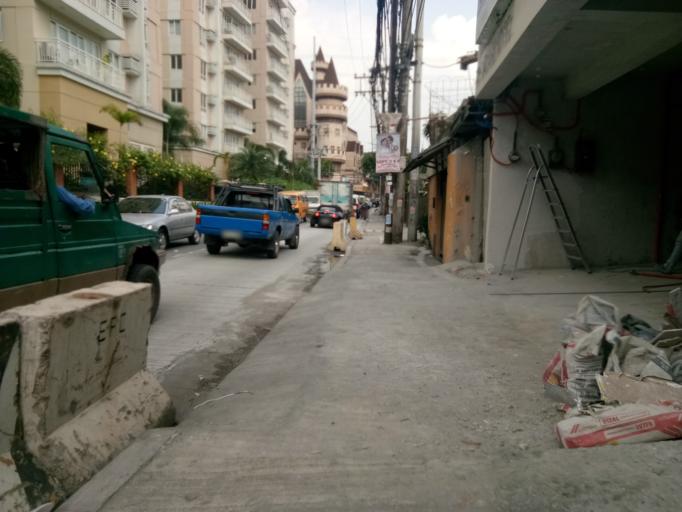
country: PH
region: Metro Manila
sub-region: San Juan
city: San Juan
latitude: 14.6141
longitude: 121.0467
